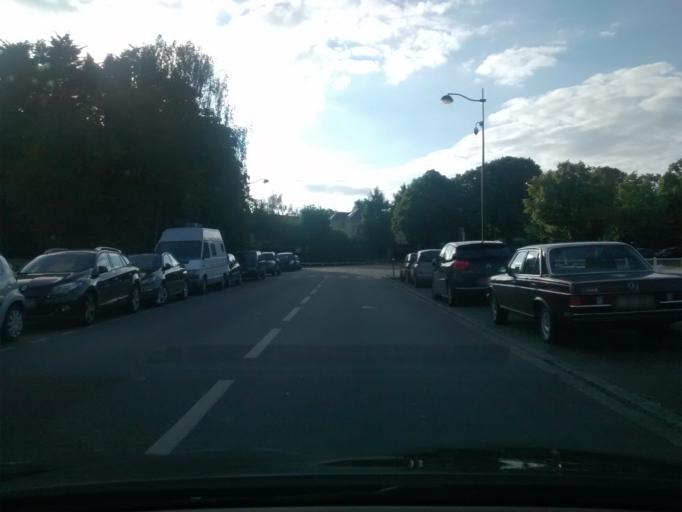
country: FR
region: Ile-de-France
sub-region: Departement des Yvelines
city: Le Chesnay
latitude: 48.8213
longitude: 2.1173
